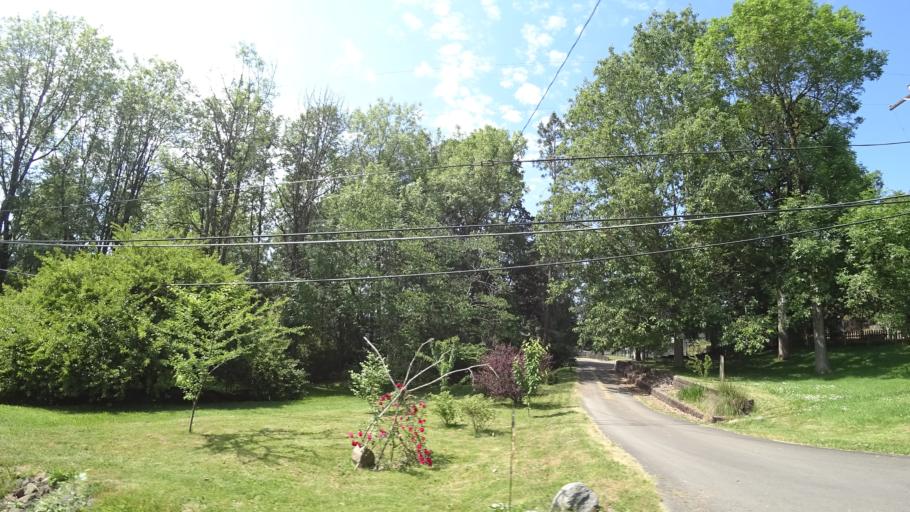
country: US
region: Oregon
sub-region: Washington County
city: Metzger
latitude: 45.4540
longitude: -122.7501
